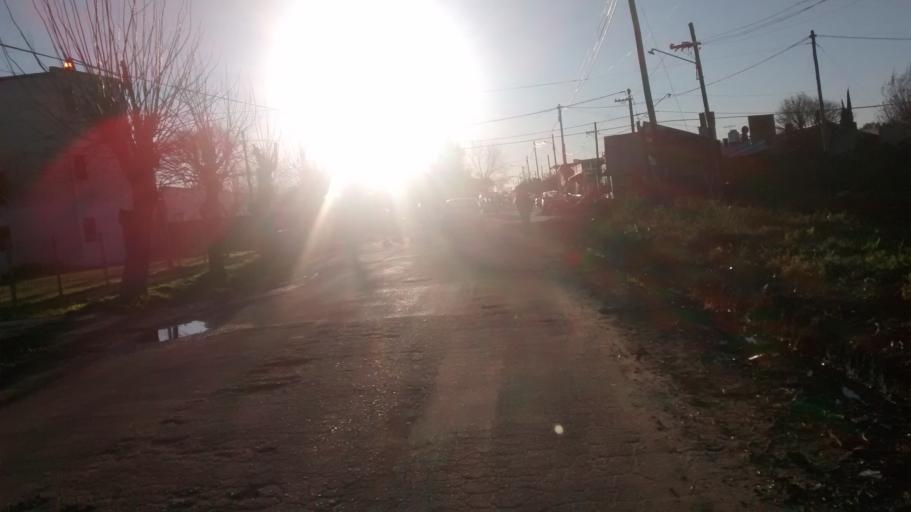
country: AR
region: Buenos Aires
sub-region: Partido de La Plata
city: La Plata
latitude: -34.9608
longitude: -57.9427
